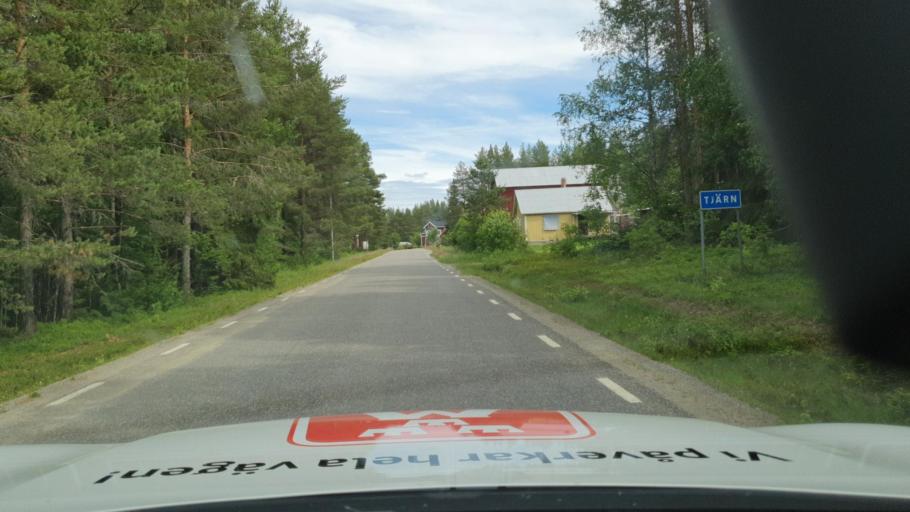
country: SE
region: Vaesterbotten
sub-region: Skelleftea Kommun
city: Viken
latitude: 64.4972
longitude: 20.9021
